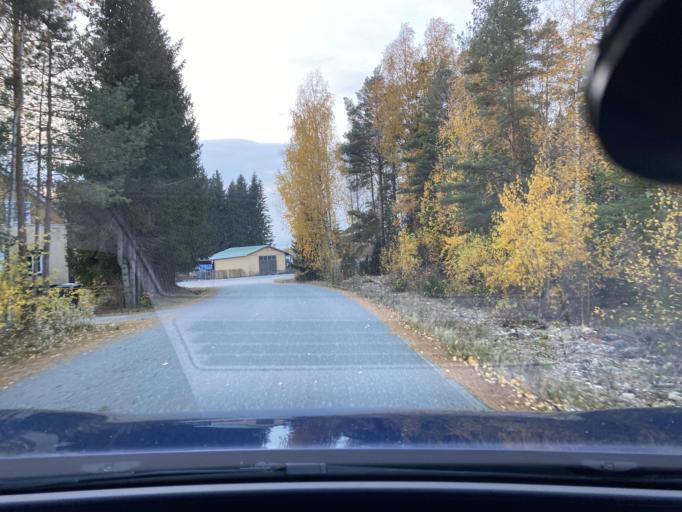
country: FI
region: Varsinais-Suomi
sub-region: Loimaa
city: Alastaro
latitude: 61.0853
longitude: 22.9188
